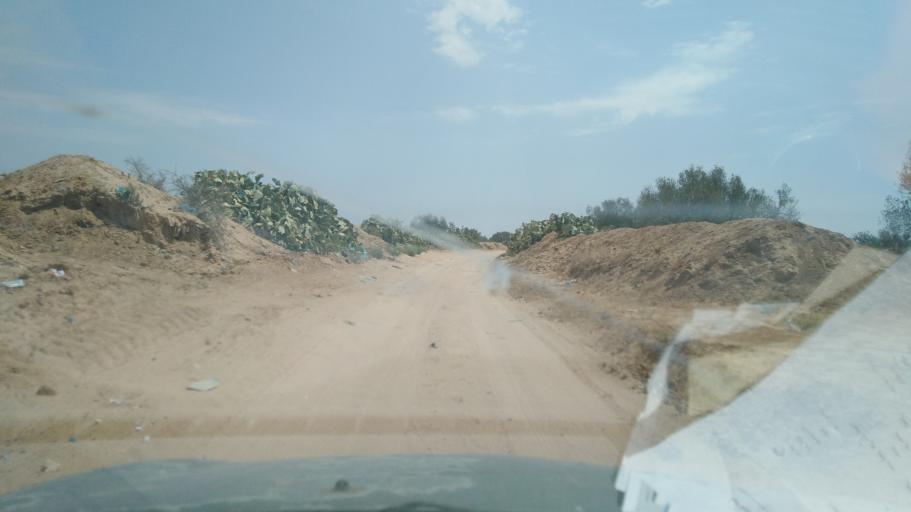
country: TN
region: Safaqis
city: Sfax
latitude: 34.7390
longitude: 10.5467
